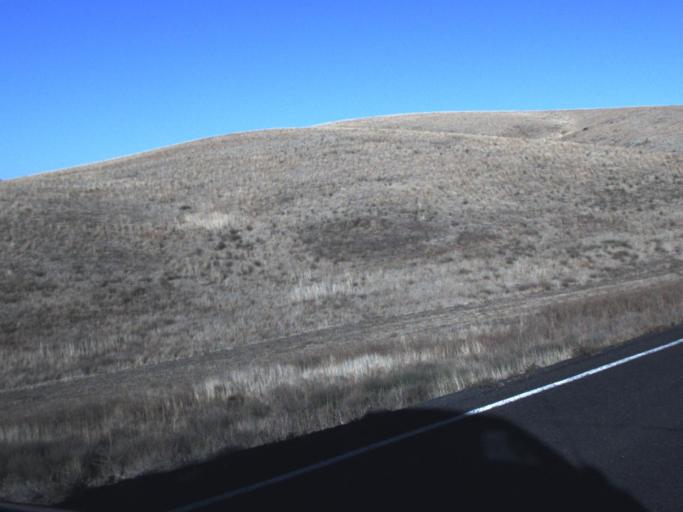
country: US
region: Washington
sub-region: Adams County
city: Ritzville
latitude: 46.6777
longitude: -118.3508
